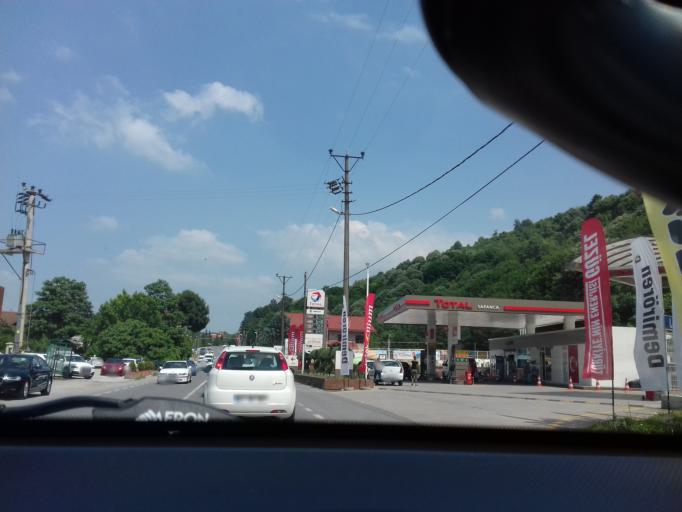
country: TR
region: Sakarya
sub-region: Merkez
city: Sapanca
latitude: 40.6908
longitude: 30.2212
